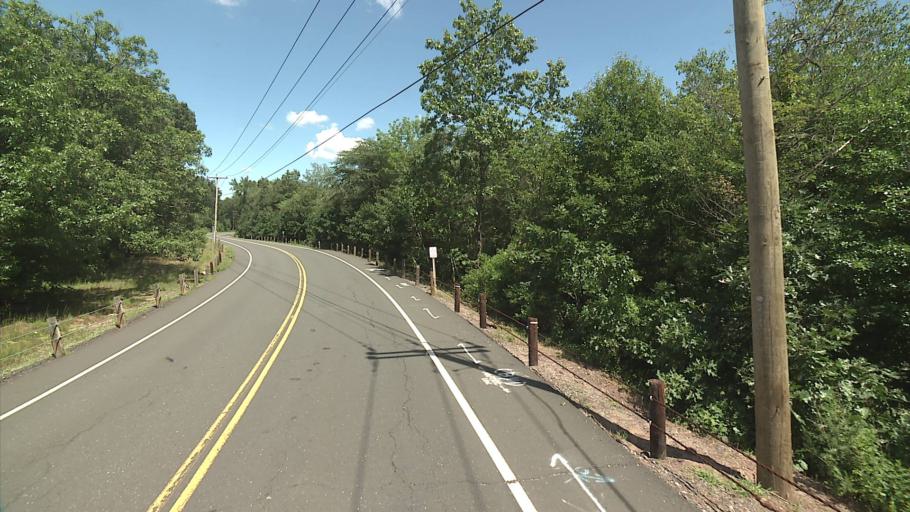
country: US
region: Massachusetts
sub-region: Hampden County
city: Southwick
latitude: 42.0208
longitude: -72.7572
